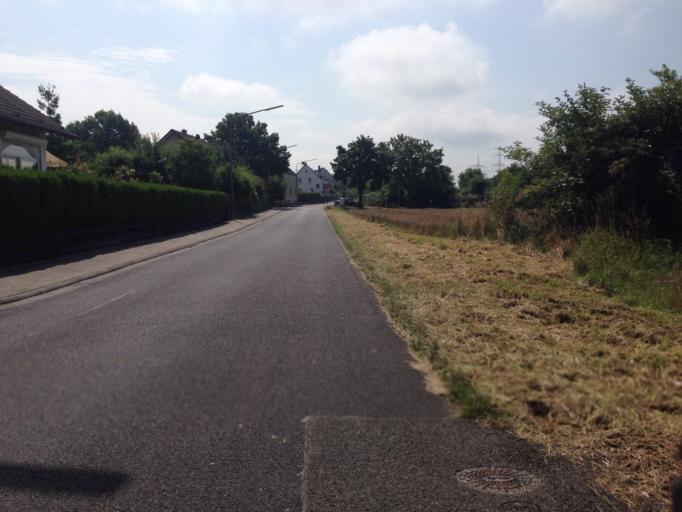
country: DE
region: Hesse
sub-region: Regierungsbezirk Darmstadt
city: Hanau am Main
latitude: 50.0951
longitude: 8.9243
